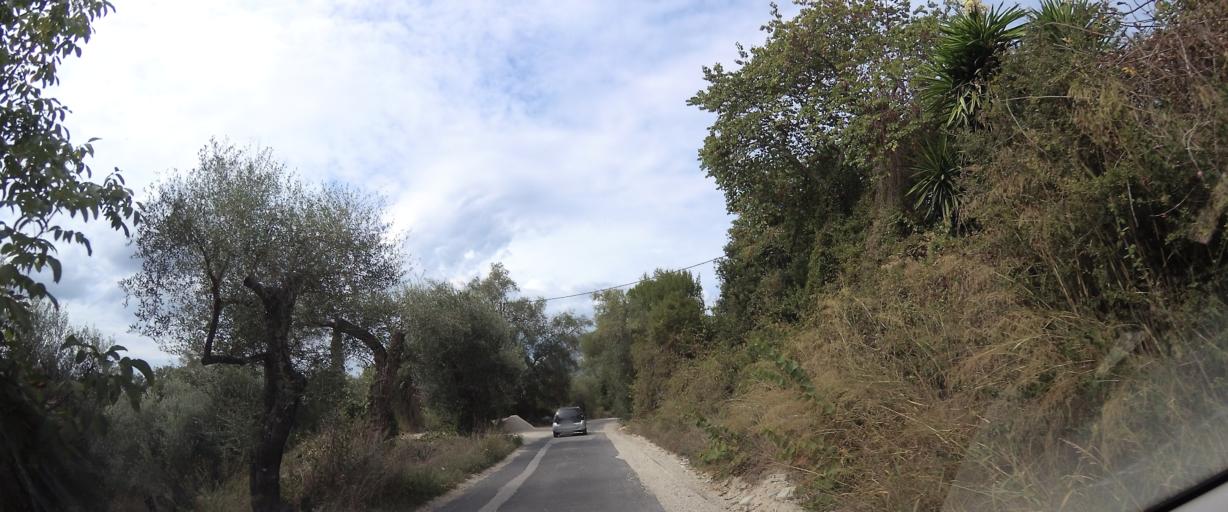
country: GR
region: Ionian Islands
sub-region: Nomos Kerkyras
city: Kontokali
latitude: 39.6934
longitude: 19.8105
